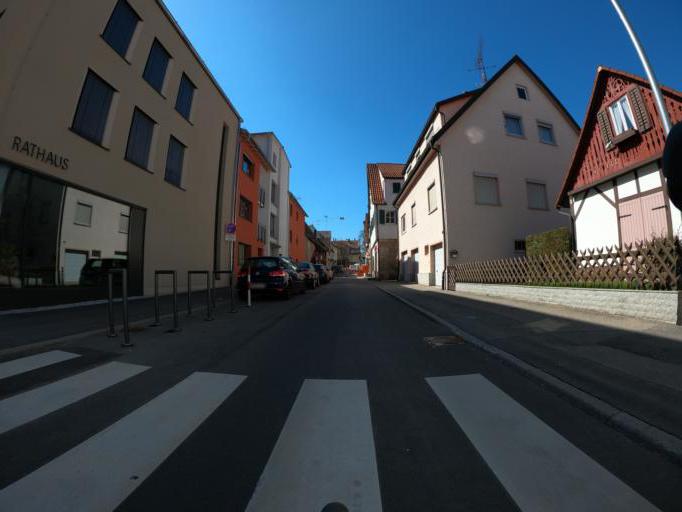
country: DE
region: Baden-Wuerttemberg
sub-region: Tuebingen Region
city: Rottenburg
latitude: 48.4776
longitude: 8.9329
